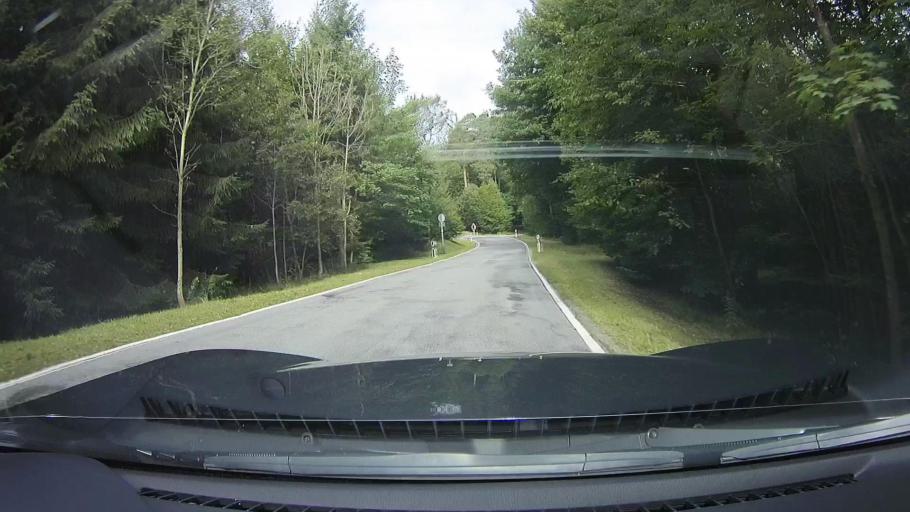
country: DE
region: Baden-Wuerttemberg
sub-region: Regierungsbezirk Stuttgart
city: Lowenstein
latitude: 49.0722
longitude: 9.3961
